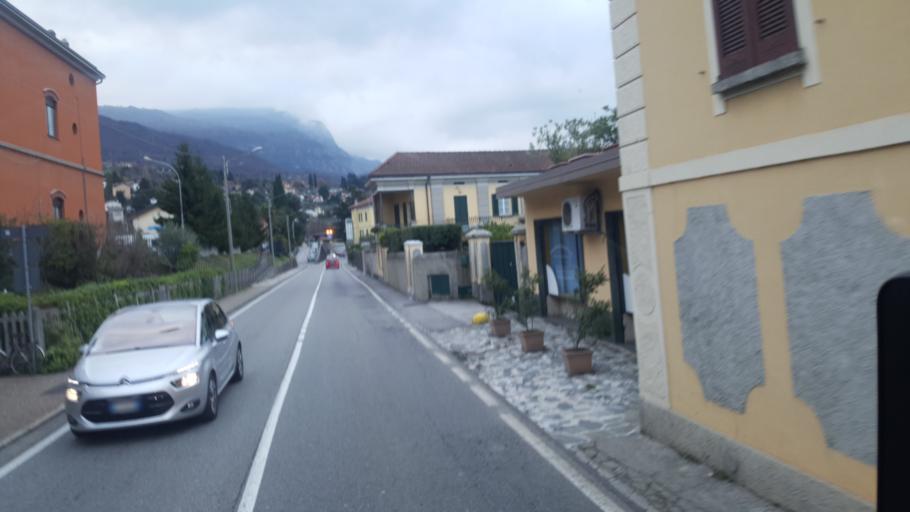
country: IT
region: Lombardy
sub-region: Provincia di Lecco
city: Mandello del Lario
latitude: 45.9162
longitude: 9.3193
